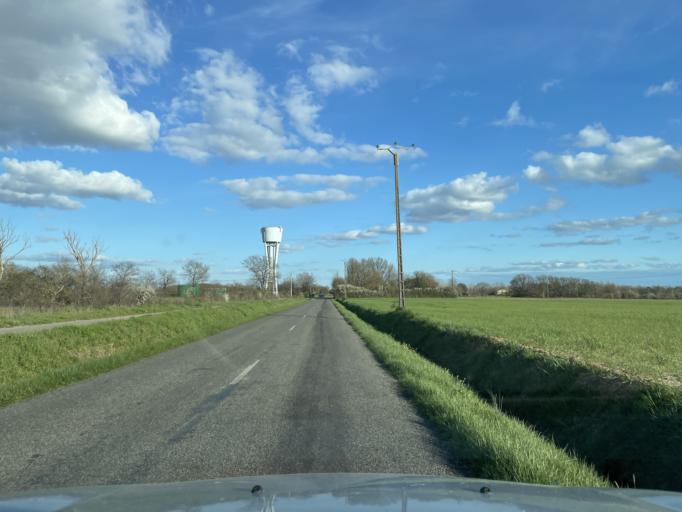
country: FR
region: Midi-Pyrenees
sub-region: Departement de la Haute-Garonne
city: Leguevin
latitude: 43.6084
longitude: 1.2135
